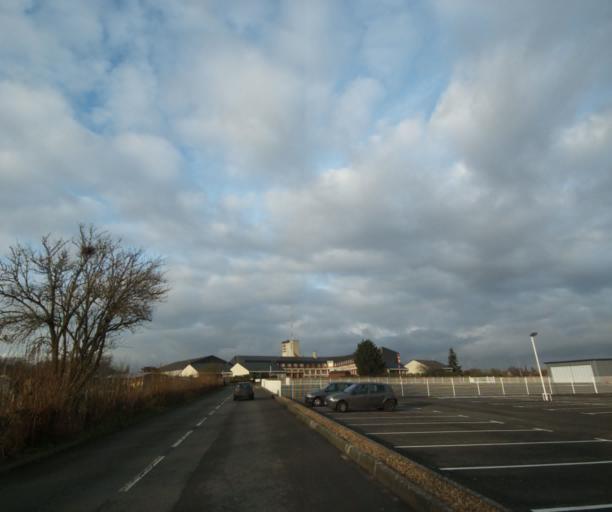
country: FR
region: Pays de la Loire
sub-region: Departement de la Sarthe
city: La Chapelle-Saint-Aubin
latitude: 48.0162
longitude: 0.1725
